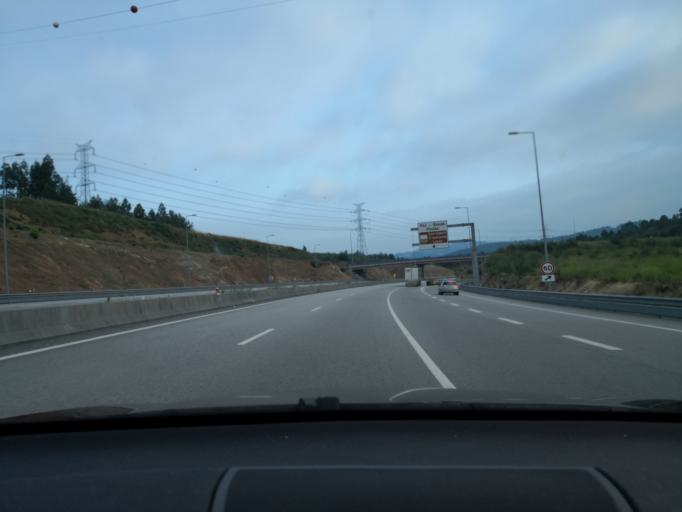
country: PT
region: Porto
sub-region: Gondomar
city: Foz do Sousa
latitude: 41.0705
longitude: -8.4514
